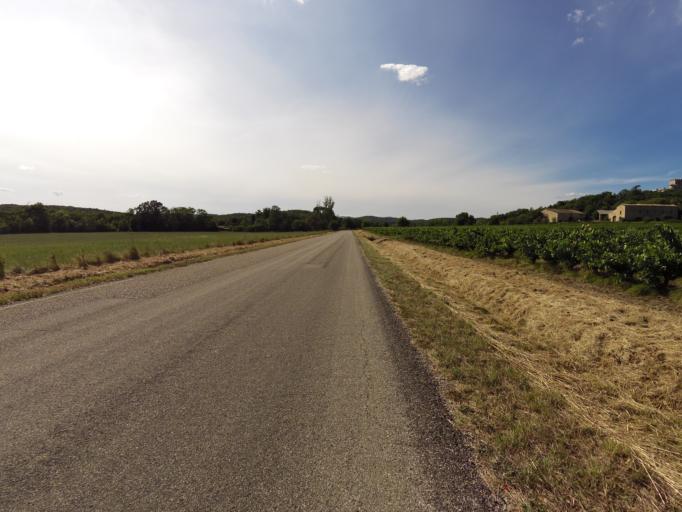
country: FR
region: Languedoc-Roussillon
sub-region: Departement du Gard
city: Sauve
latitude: 43.9843
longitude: 3.9815
